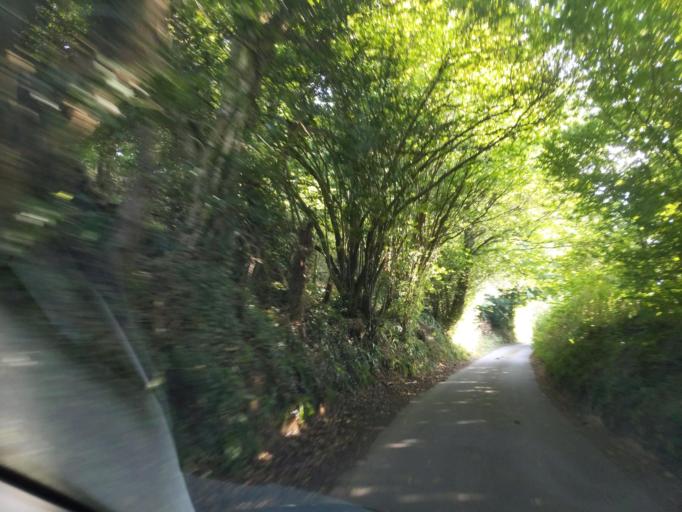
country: GB
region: England
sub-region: Devon
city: Winkleigh
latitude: 50.9675
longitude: -3.9768
